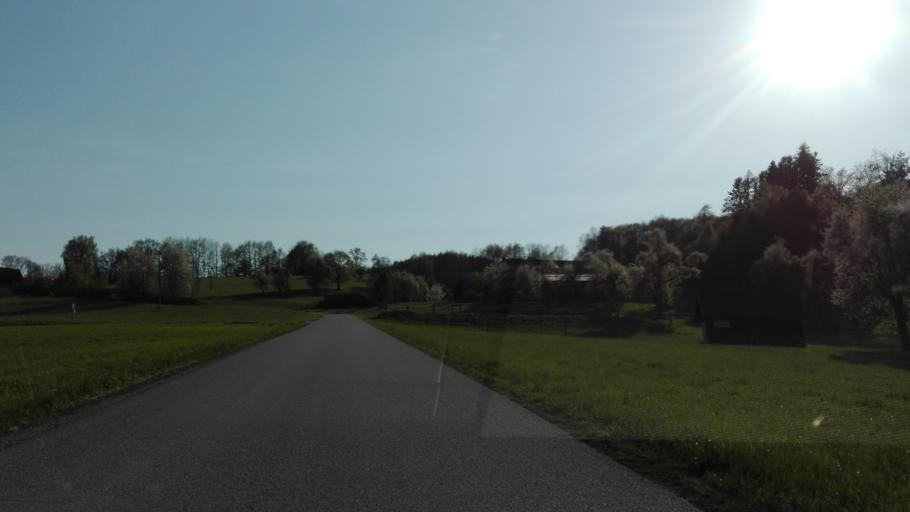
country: AT
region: Upper Austria
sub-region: Politischer Bezirk Grieskirchen
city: Grieskirchen
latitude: 48.3664
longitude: 13.7900
